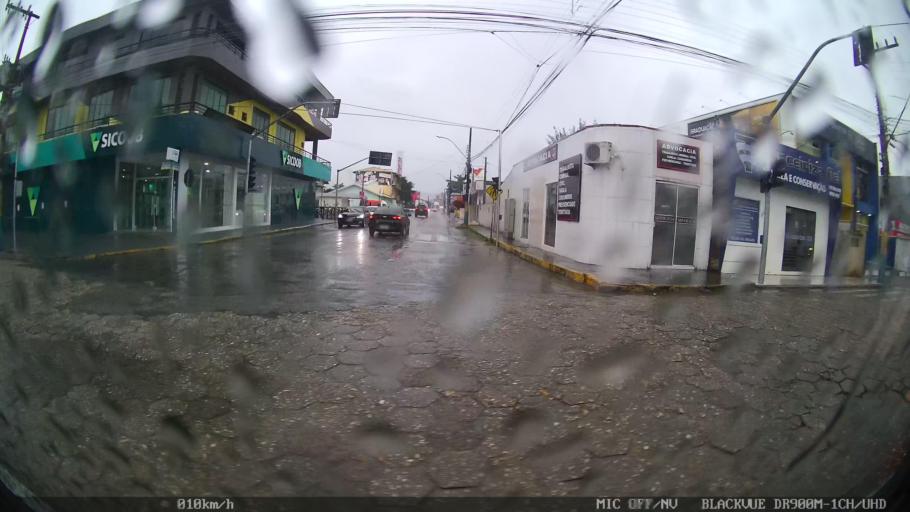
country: BR
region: Santa Catarina
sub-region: Navegantes
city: Navegantes
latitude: -26.8956
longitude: -48.6549
